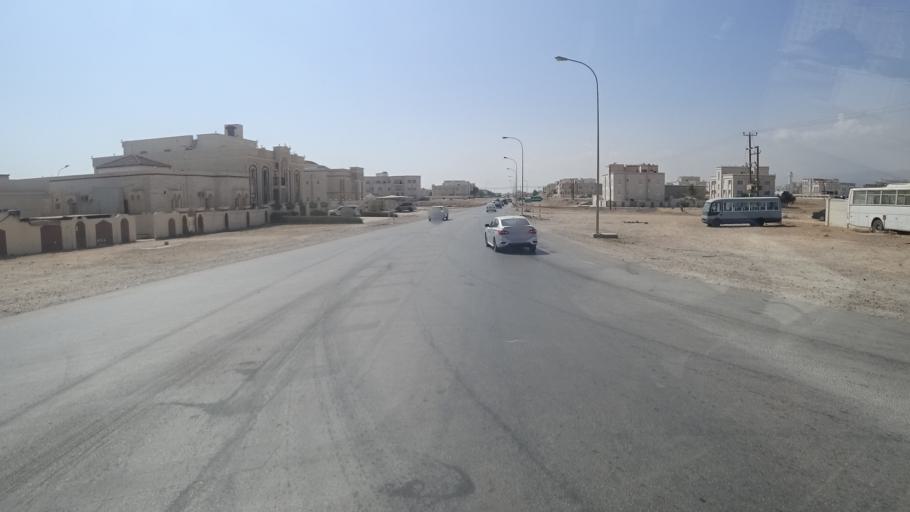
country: OM
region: Zufar
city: Salalah
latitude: 17.0197
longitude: 54.0325
